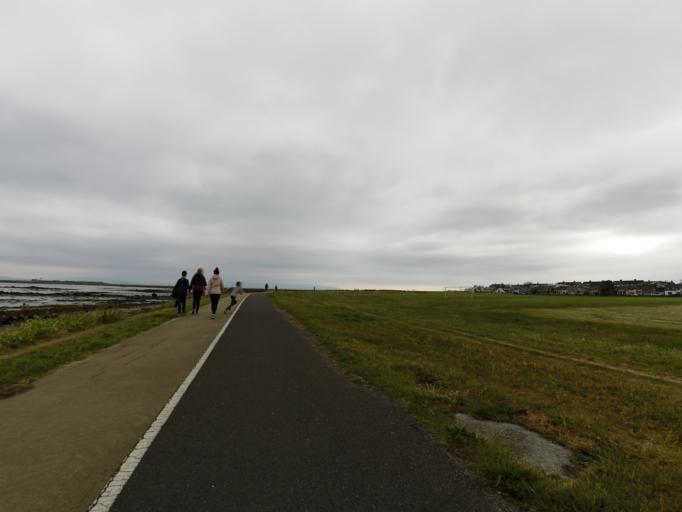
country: IE
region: Connaught
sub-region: County Galway
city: Gaillimh
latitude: 53.2648
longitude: -9.0518
